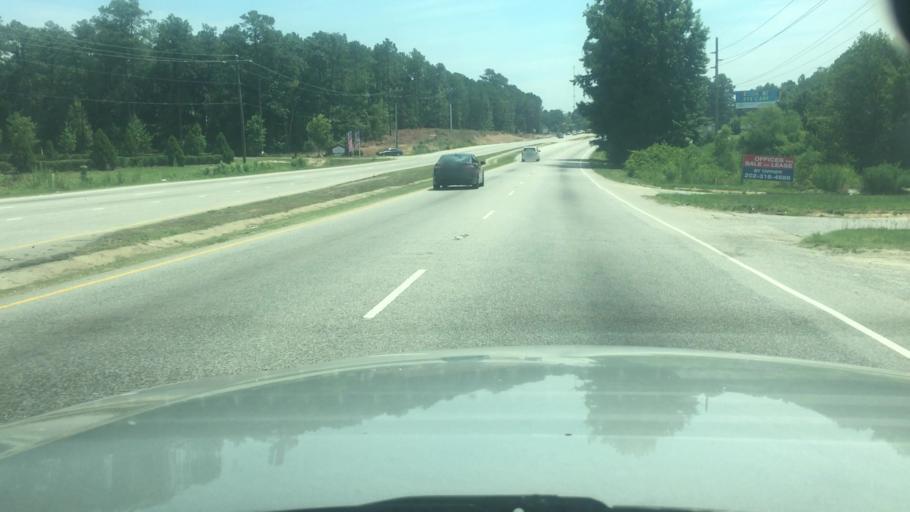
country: US
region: North Carolina
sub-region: Hoke County
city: Rockfish
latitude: 35.0406
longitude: -78.9960
